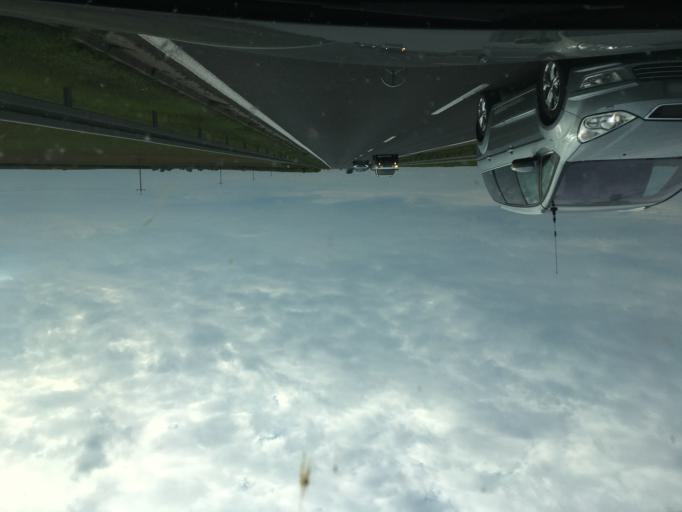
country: PL
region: Podlasie
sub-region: Powiat kolnenski
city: Stawiski
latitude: 53.4138
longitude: 22.1631
